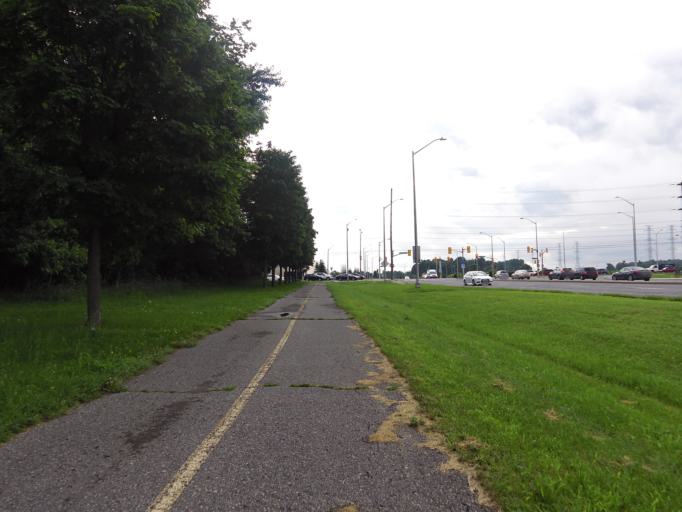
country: CA
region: Ontario
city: Bells Corners
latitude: 45.3218
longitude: -75.7784
